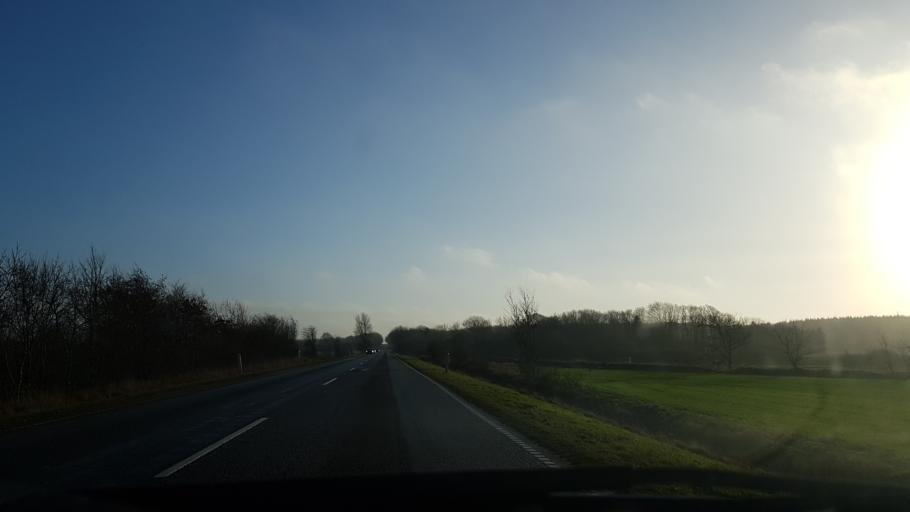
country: DK
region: South Denmark
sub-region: Tonder Kommune
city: Toftlund
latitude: 55.2293
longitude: 9.1706
